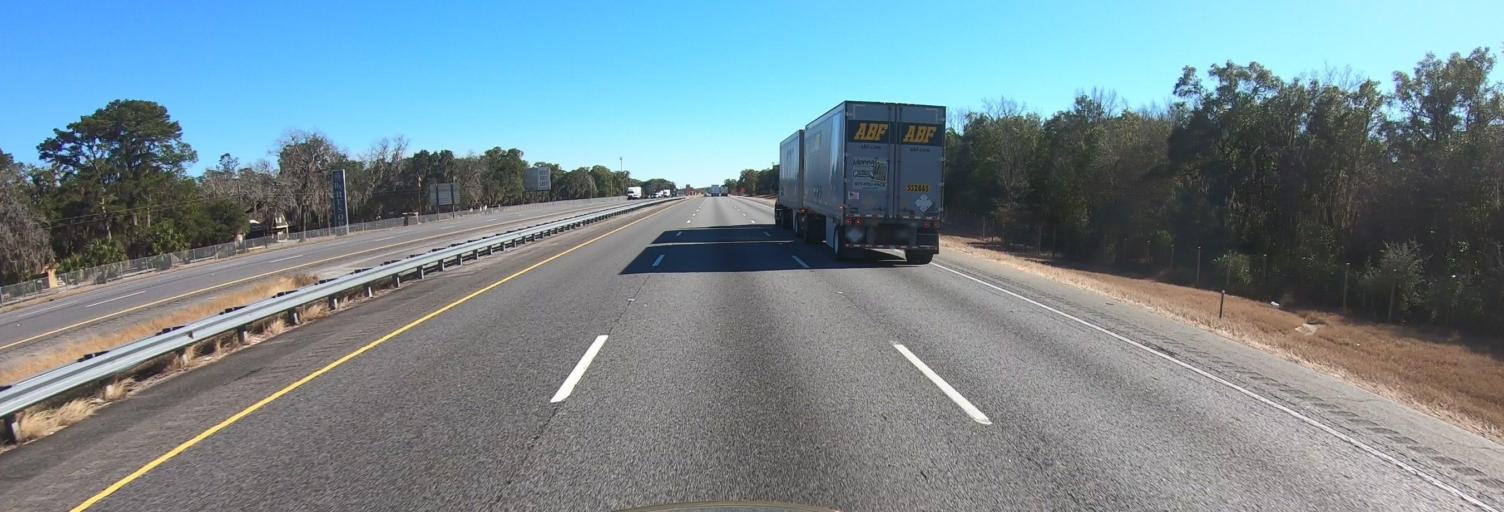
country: US
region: Georgia
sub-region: Lowndes County
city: Valdosta
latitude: 30.6702
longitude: -83.2141
